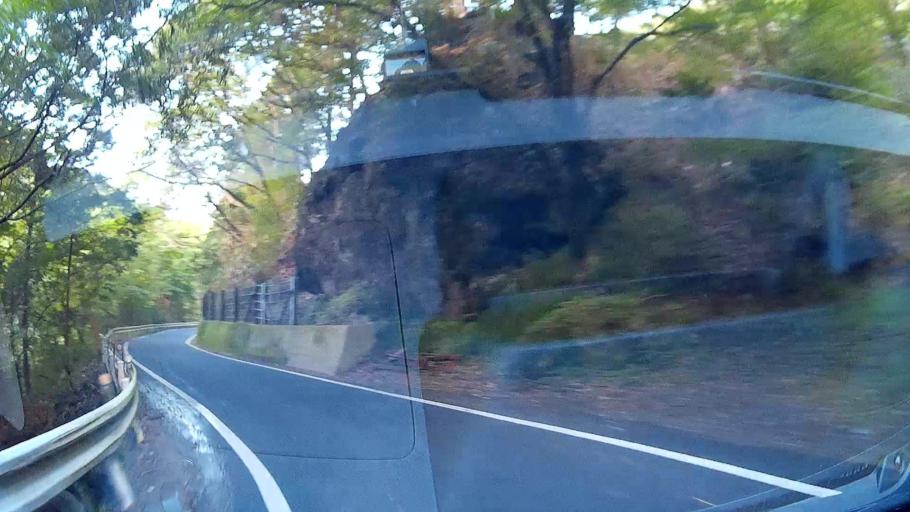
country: JP
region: Shizuoka
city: Shizuoka-shi
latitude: 35.1354
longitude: 138.2728
